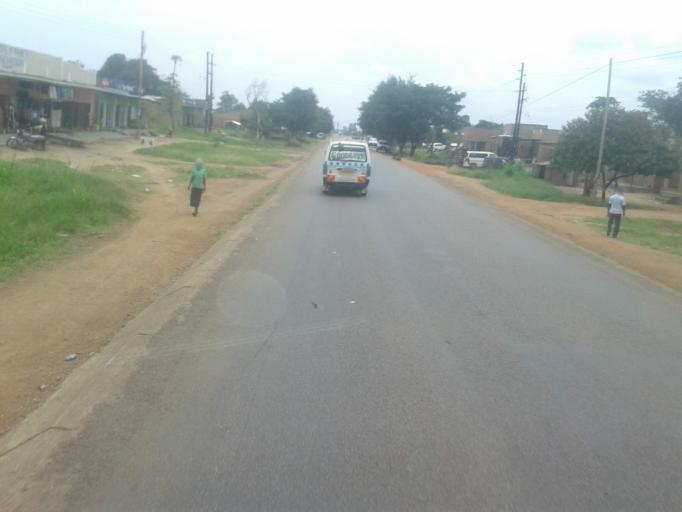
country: UG
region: Western Region
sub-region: Kiryandongo District
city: Masindi Port
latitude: 1.5328
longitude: 32.0427
